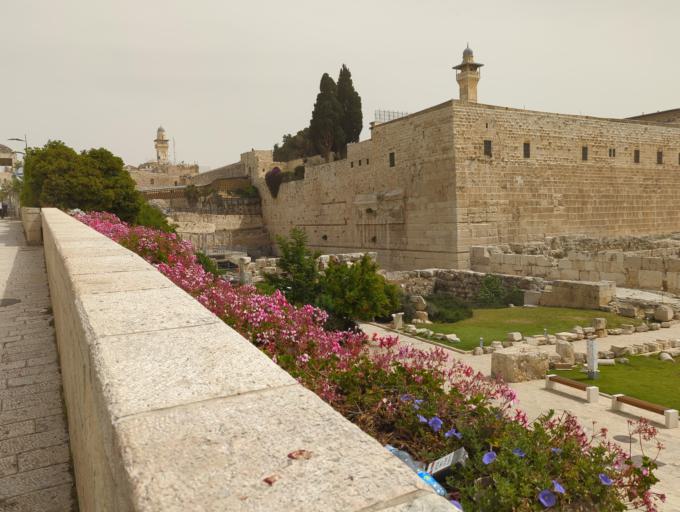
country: PS
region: West Bank
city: Old City
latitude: 31.7750
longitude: 35.2342
